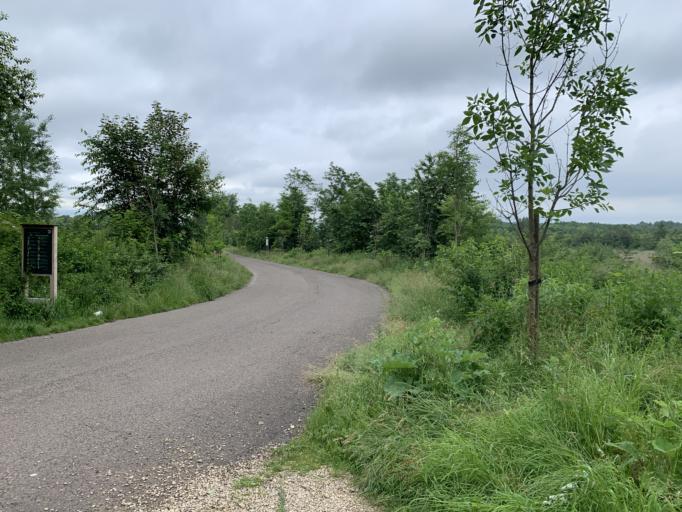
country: PL
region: Silesian Voivodeship
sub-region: Bytom
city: Bytom
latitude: 50.3288
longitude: 18.9507
